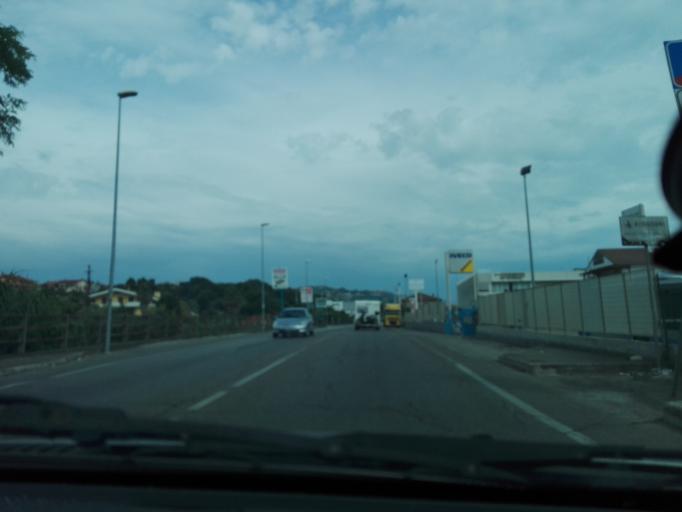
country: IT
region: Abruzzo
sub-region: Provincia di Pescara
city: San Martino Bassa
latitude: 42.5304
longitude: 14.1331
